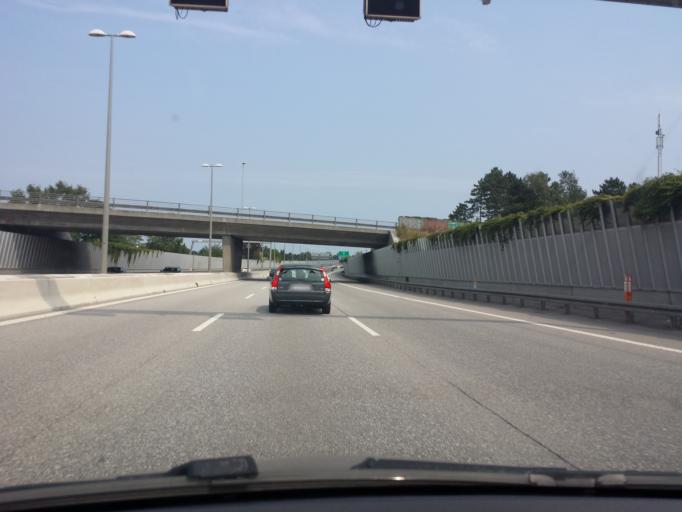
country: DK
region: Capital Region
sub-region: Gladsaxe Municipality
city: Buddinge
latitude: 55.7451
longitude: 12.4616
